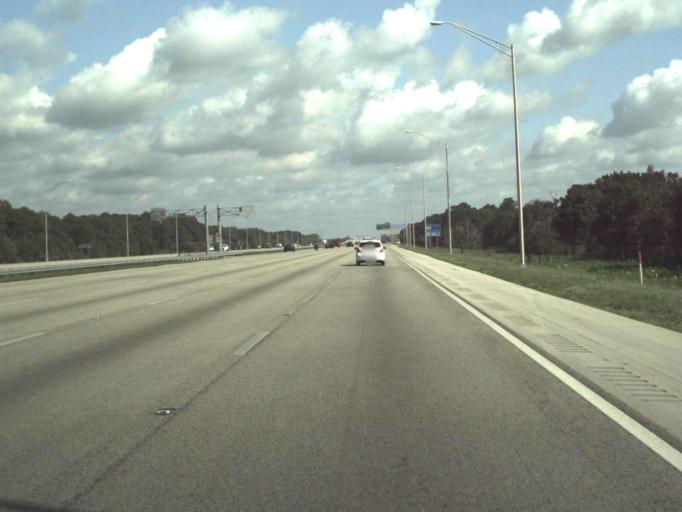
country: US
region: Florida
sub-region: Palm Beach County
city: Palm Beach Gardens
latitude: 26.8669
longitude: -80.1187
